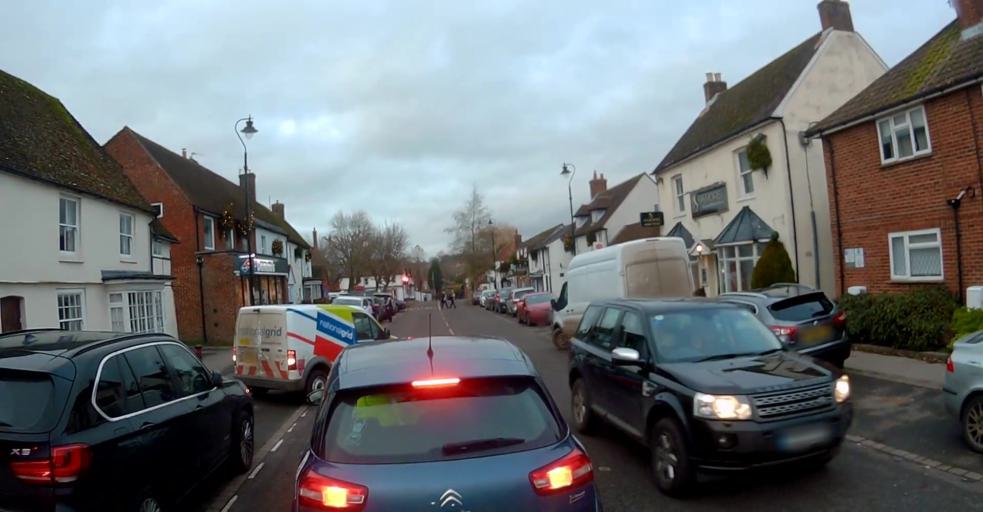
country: GB
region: England
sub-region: Hampshire
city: Overton
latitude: 51.2431
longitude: -1.2630
